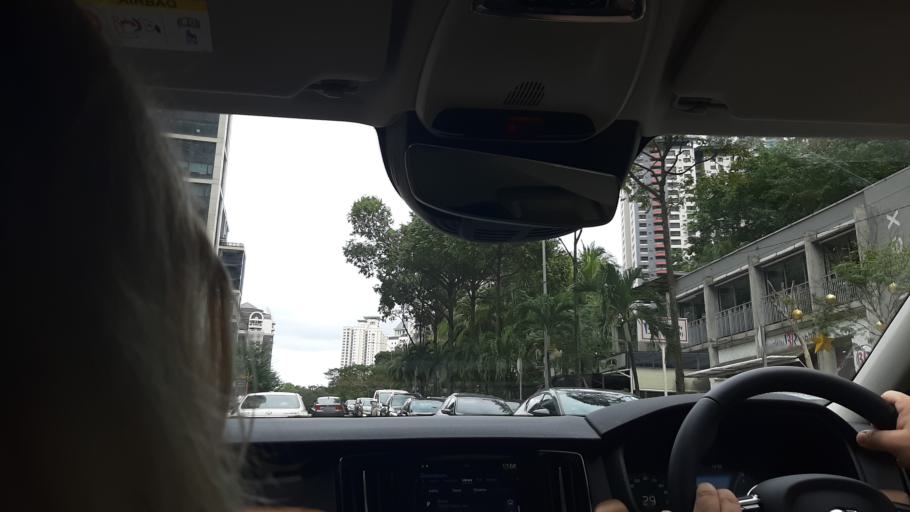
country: MY
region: Kuala Lumpur
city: Kuala Lumpur
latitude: 3.1661
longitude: 101.6529
